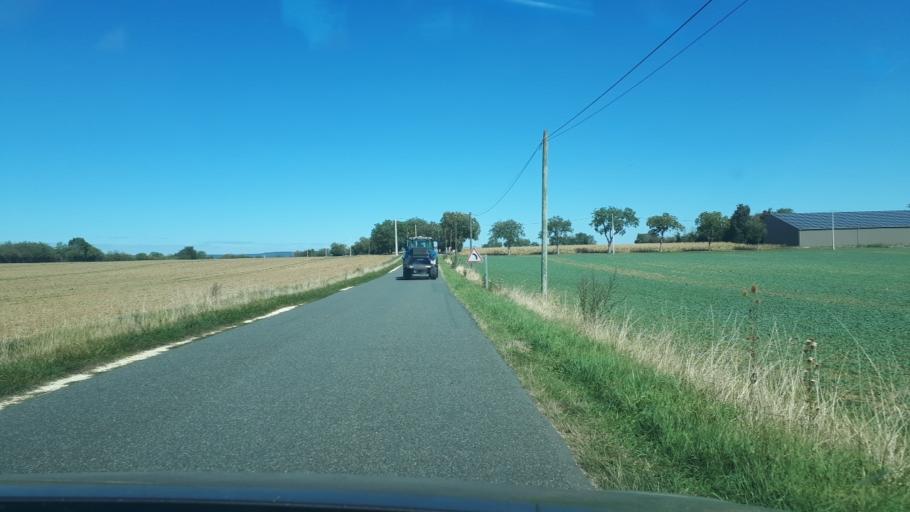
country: FR
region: Centre
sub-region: Departement du Cher
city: Sainte-Solange
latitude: 47.1593
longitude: 2.5663
